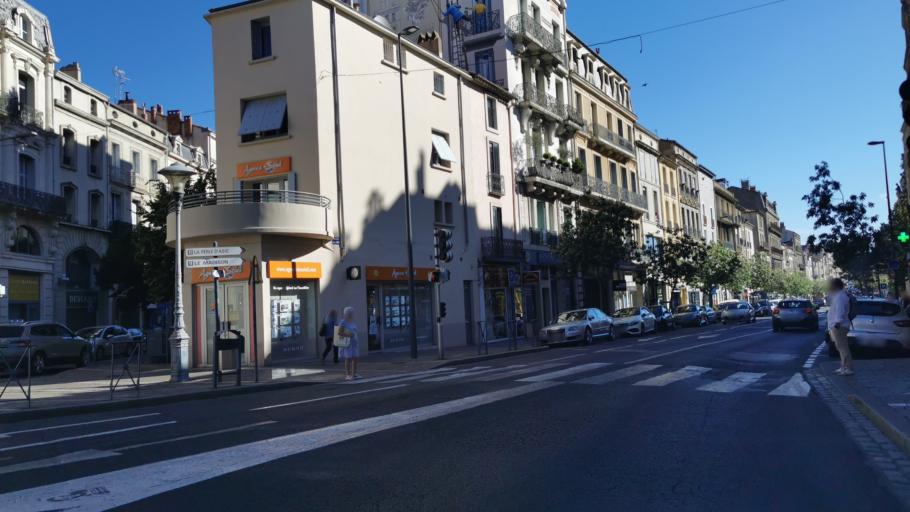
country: FR
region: Languedoc-Roussillon
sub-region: Departement de l'Herault
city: Beziers
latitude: 43.3450
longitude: 3.2157
